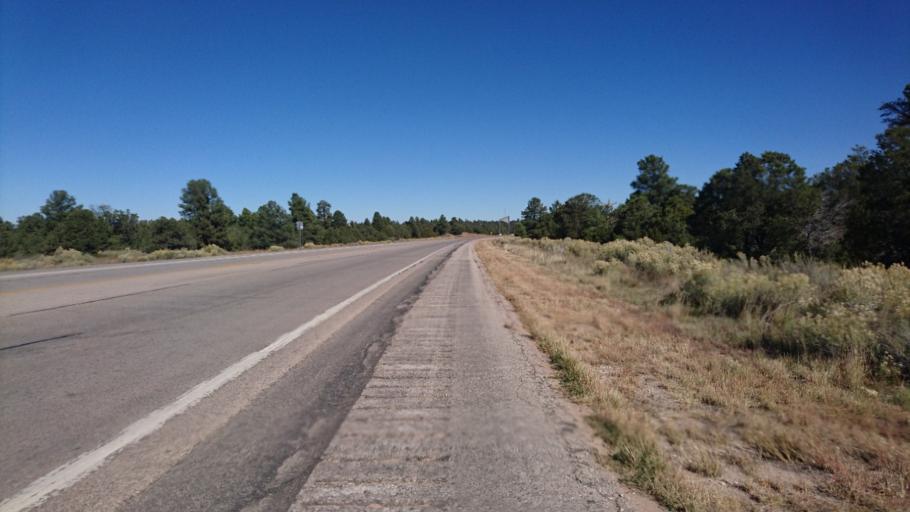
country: US
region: New Mexico
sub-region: McKinley County
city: Black Rock
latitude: 35.2296
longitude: -108.7662
